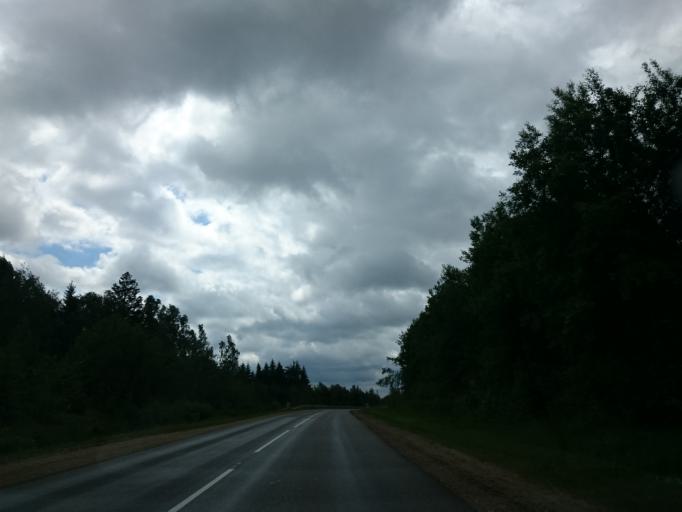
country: LV
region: Madonas Rajons
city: Madona
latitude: 56.8757
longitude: 26.1782
